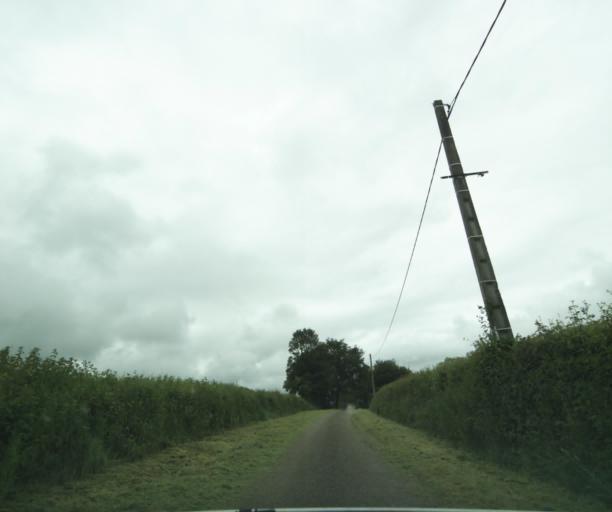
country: FR
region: Bourgogne
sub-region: Departement de Saone-et-Loire
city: Charolles
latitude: 46.4642
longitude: 4.3525
